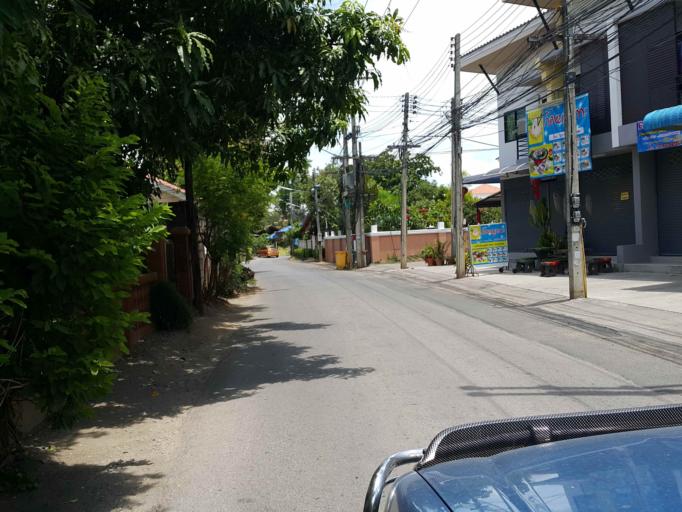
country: TH
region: Chiang Mai
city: Chiang Mai
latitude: 18.7696
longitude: 99.0261
